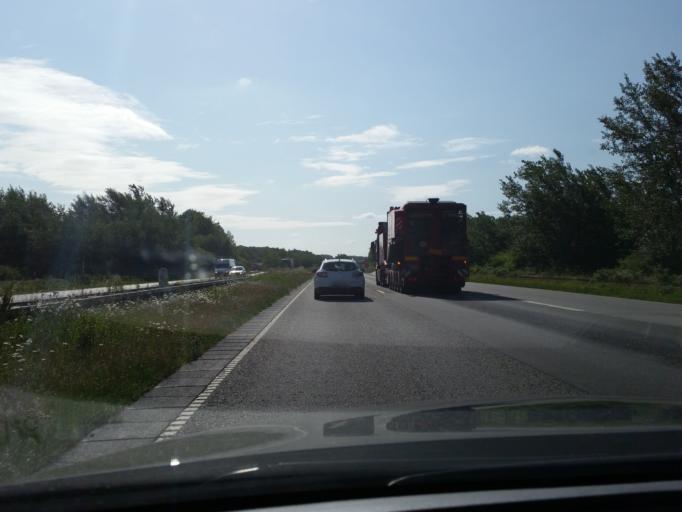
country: DK
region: South Denmark
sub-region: Assens Kommune
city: Vissenbjerg
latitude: 55.3960
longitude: 10.1819
